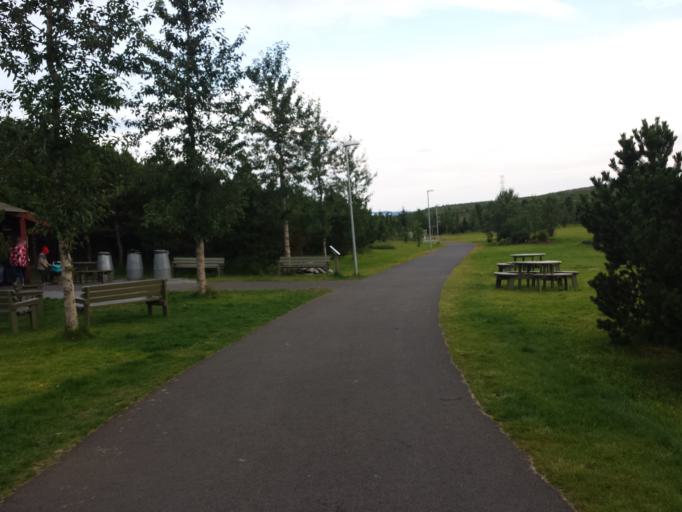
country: IS
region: Capital Region
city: Reykjavik
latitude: 64.0739
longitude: -21.8243
